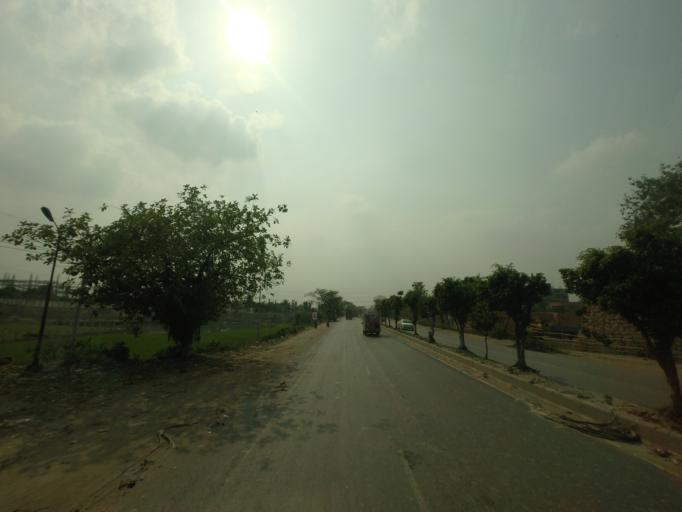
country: BD
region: Dhaka
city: Azimpur
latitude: 23.7898
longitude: 90.3180
